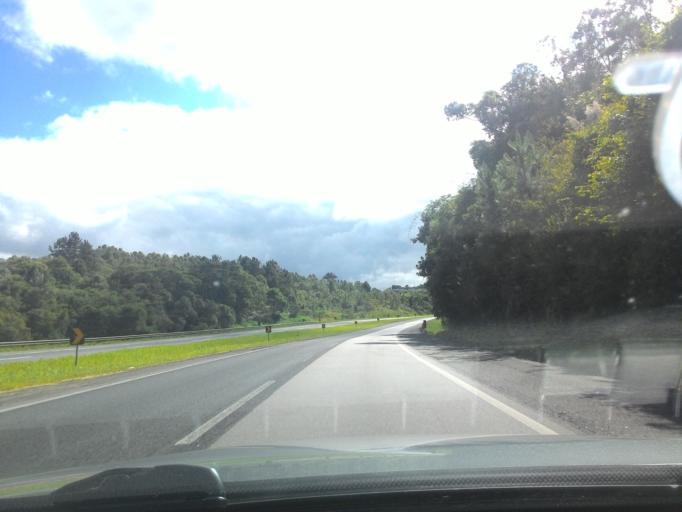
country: BR
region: Sao Paulo
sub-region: Cajati
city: Cajati
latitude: -24.9509
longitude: -48.3161
